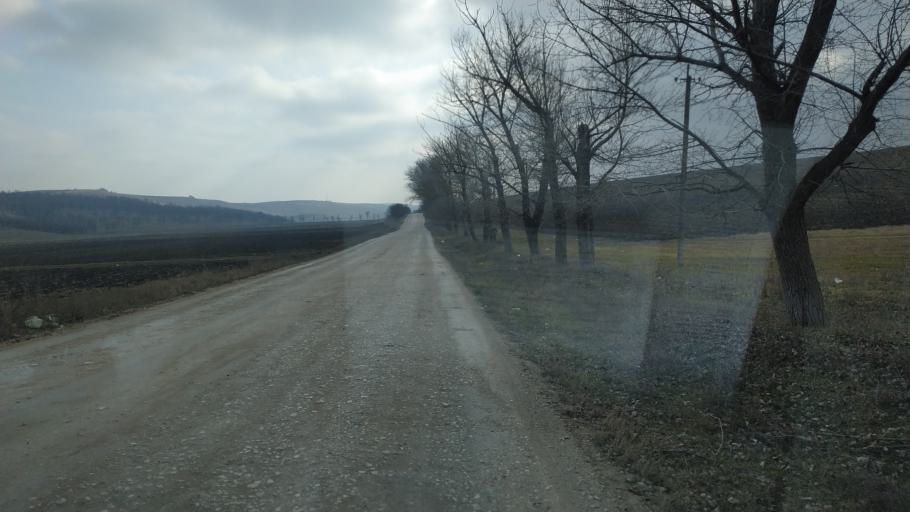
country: MD
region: Hincesti
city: Dancu
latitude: 46.9291
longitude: 28.3277
